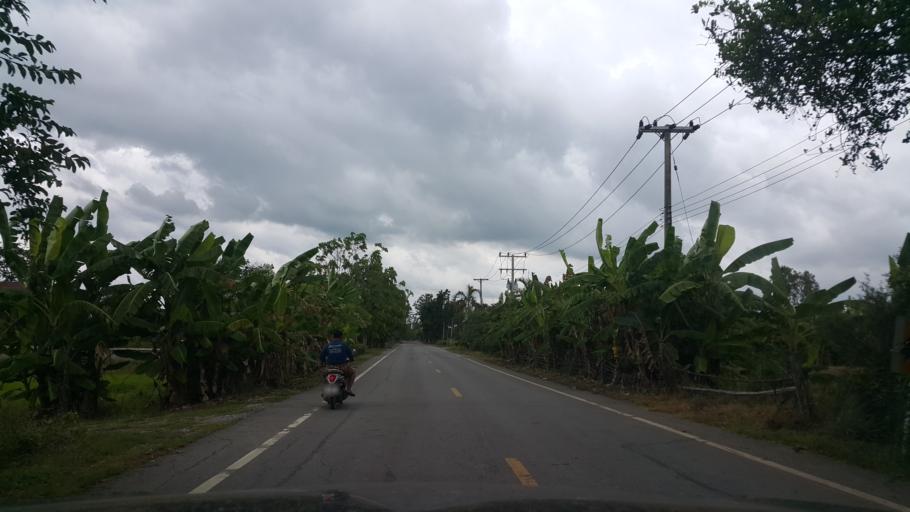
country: TH
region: Sukhothai
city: Kong Krailat
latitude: 16.9228
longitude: 99.8887
